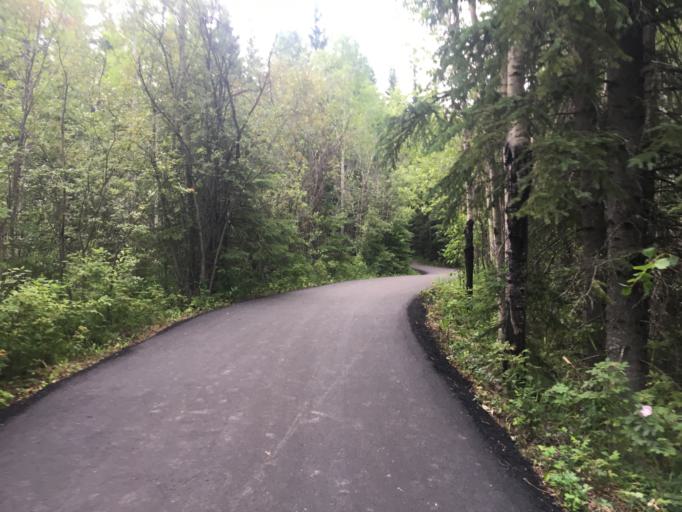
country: CA
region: Alberta
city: Grande Prairie
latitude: 55.1337
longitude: -118.7888
